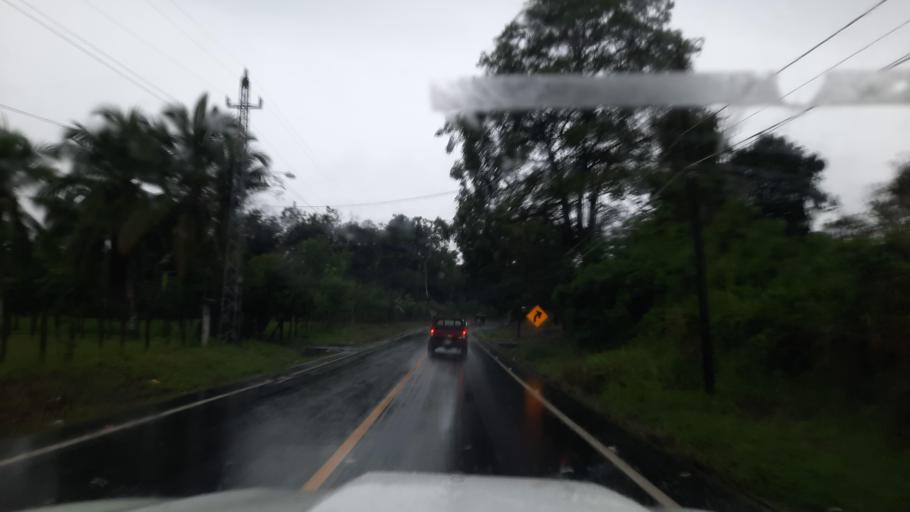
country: PA
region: Chiriqui
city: La Concepcion
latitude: 8.5379
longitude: -82.6235
